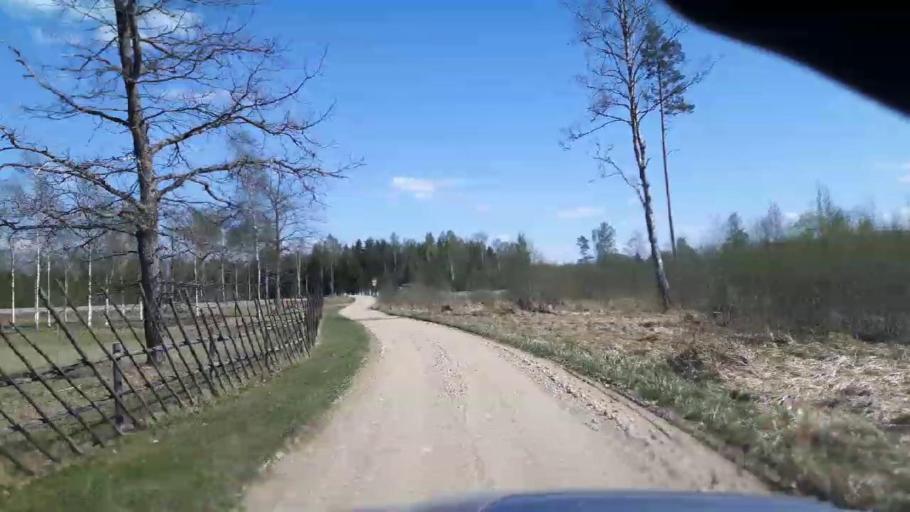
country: EE
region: Paernumaa
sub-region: Tootsi vald
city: Tootsi
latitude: 58.5412
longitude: 24.8112
